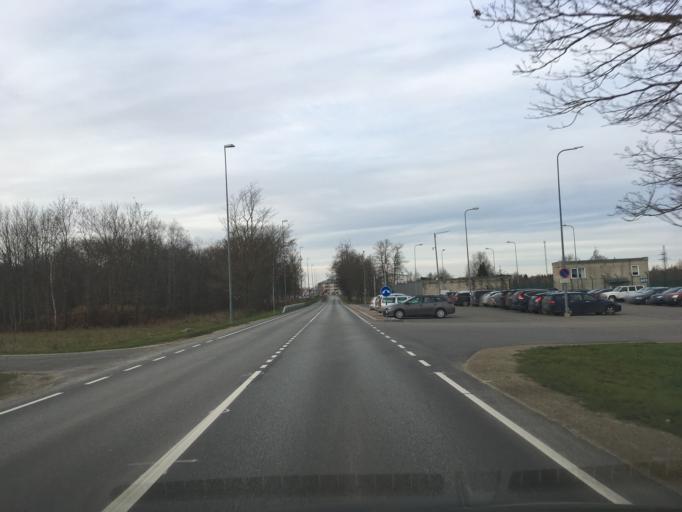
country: EE
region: Ida-Virumaa
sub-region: Johvi vald
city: Johvi
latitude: 59.3489
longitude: 27.4344
